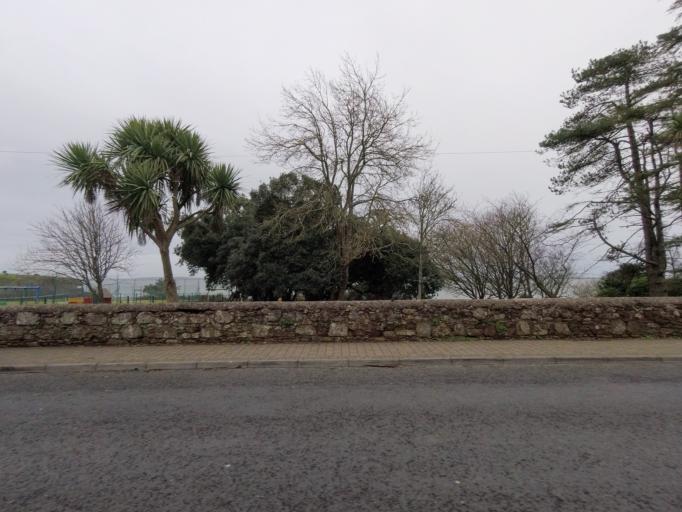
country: IE
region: Munster
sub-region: Waterford
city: Dunmore East
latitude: 52.1508
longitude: -6.9945
